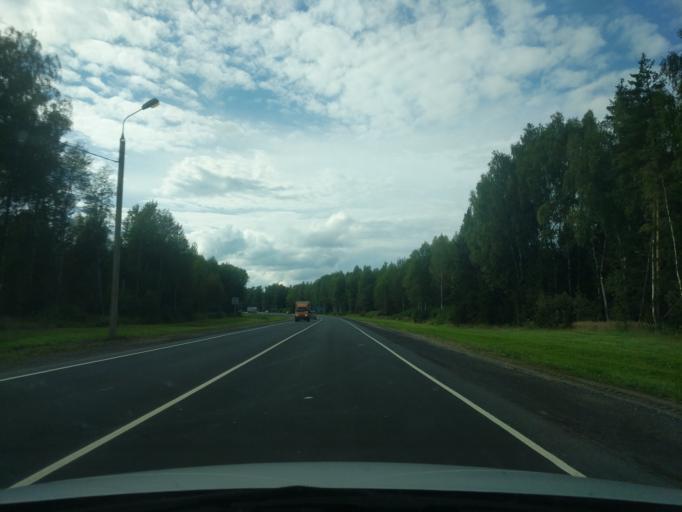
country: RU
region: Jaroslavl
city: Nekrasovskoye
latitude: 57.6368
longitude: 40.3983
